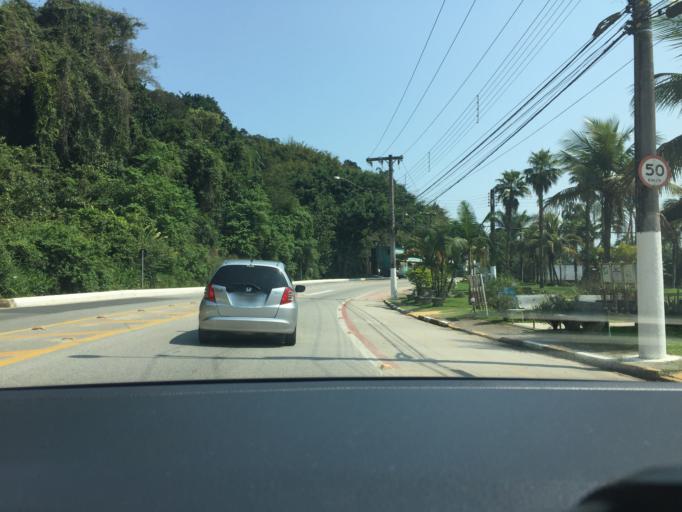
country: BR
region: Sao Paulo
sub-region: Guaruja
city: Guaruja
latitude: -23.9788
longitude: -46.1900
